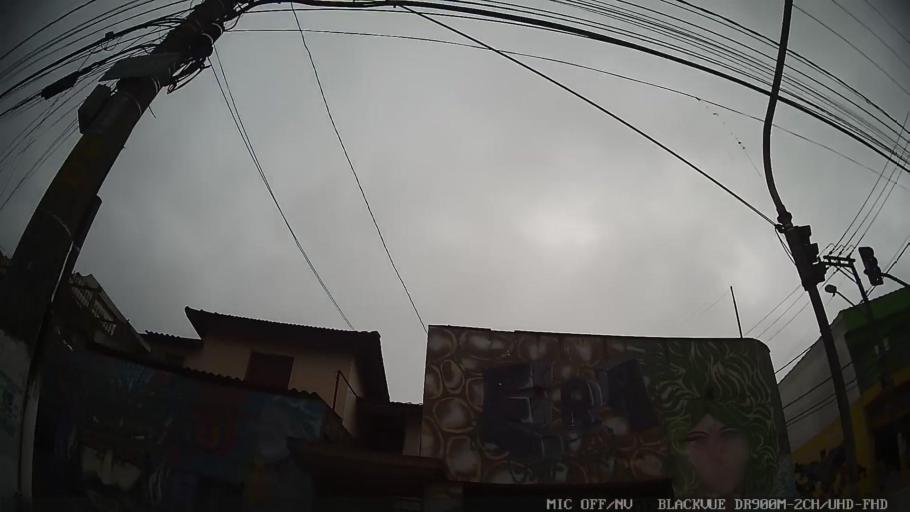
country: BR
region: Sao Paulo
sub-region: Osasco
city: Osasco
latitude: -23.4549
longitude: -46.7493
